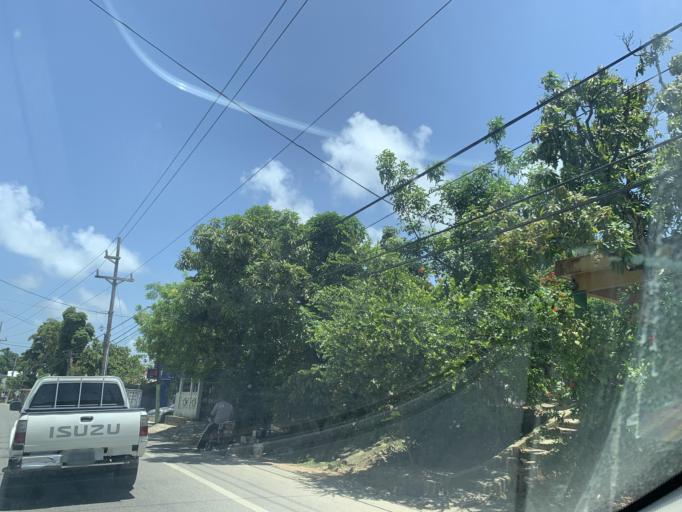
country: DO
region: Puerto Plata
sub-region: Puerto Plata
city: Puerto Plata
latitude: 19.7474
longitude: -70.5891
